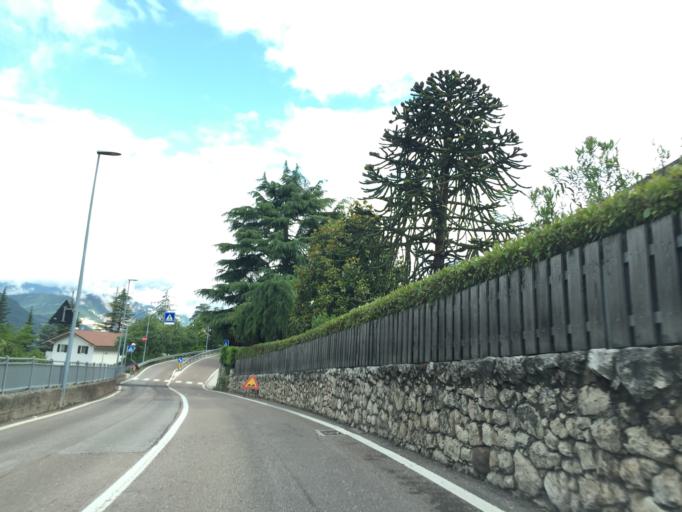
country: IT
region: Trentino-Alto Adige
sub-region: Provincia di Trento
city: Povo
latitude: 46.0408
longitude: 11.1420
